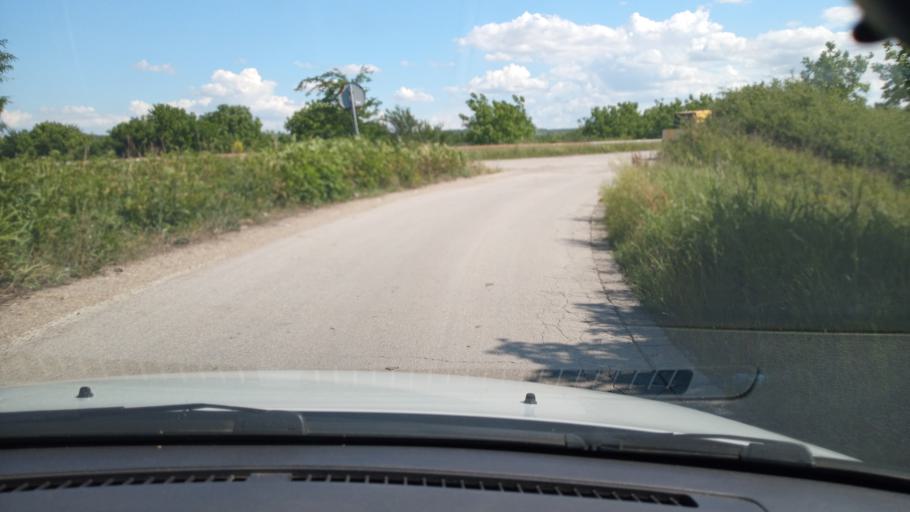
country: BG
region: Pleven
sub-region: Obshtina Dolna Mitropoliya
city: Dolna Mitropoliya
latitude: 43.4393
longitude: 24.5270
